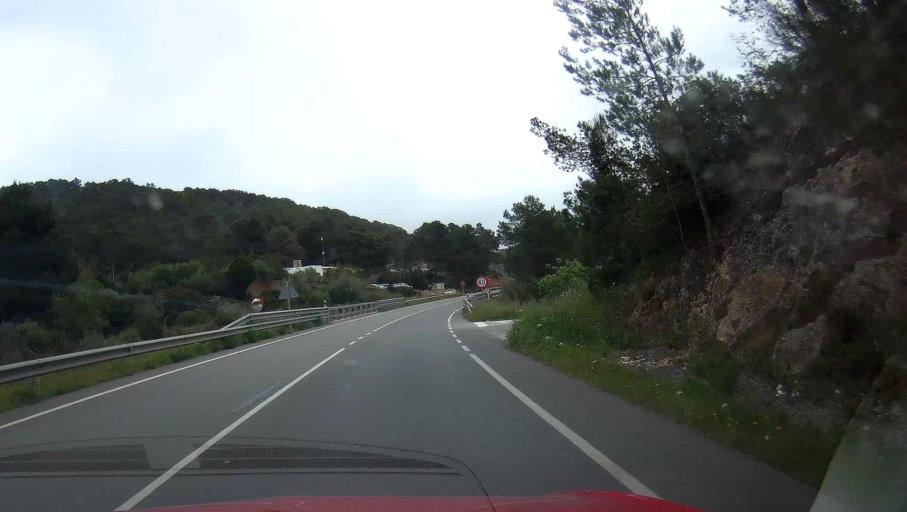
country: ES
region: Balearic Islands
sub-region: Illes Balears
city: Sant Joan de Labritja
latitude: 39.0760
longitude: 1.5023
